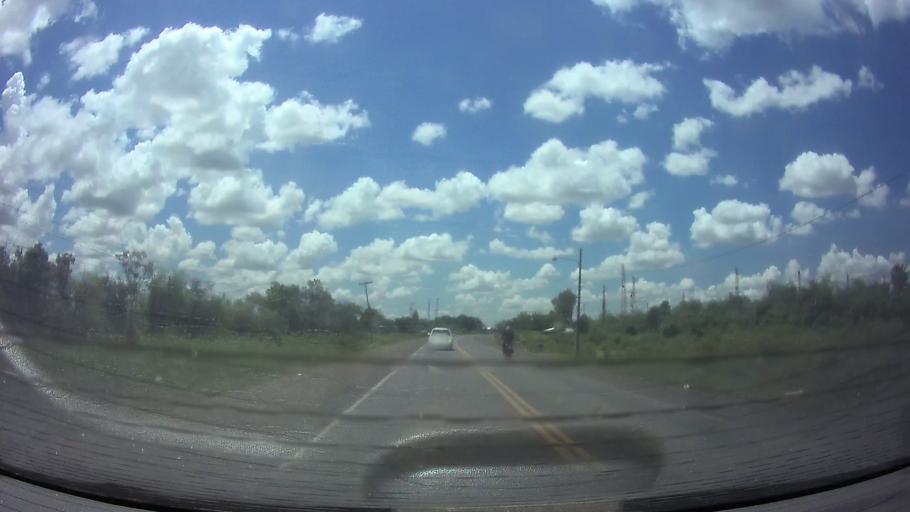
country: PY
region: Presidente Hayes
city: Nanawa
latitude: -25.2307
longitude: -57.6918
